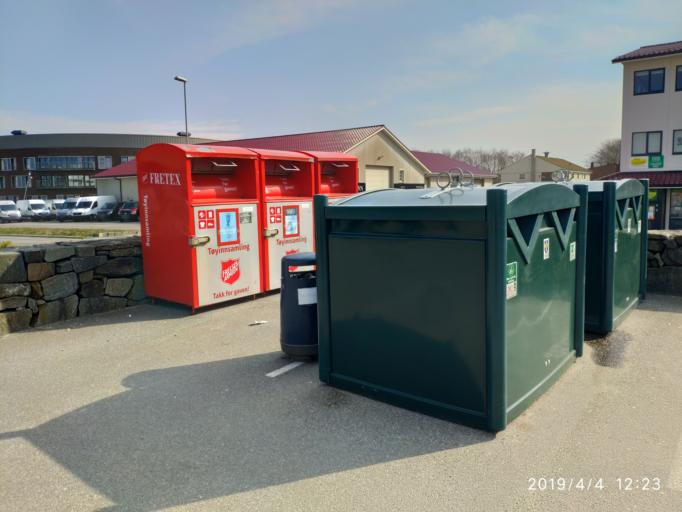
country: NO
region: Rogaland
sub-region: Klepp
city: Kleppe
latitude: 58.7787
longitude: 5.6278
